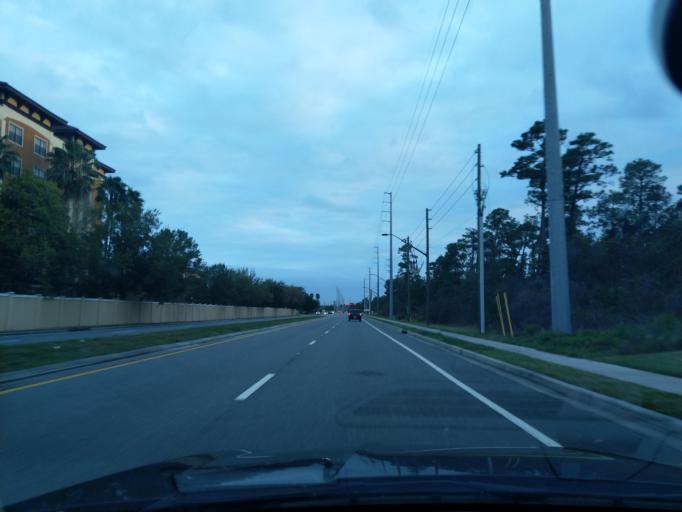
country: US
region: Florida
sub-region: Orange County
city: Williamsburg
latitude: 28.3899
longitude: -81.4832
